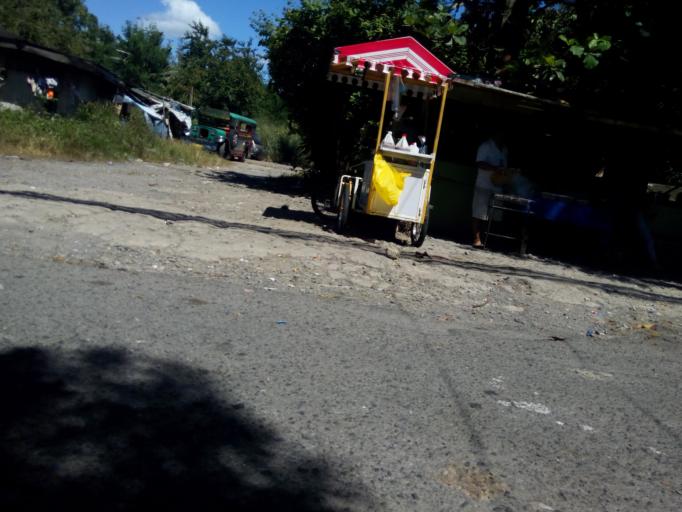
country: PH
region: Metro Manila
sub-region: Quezon City
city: Quezon City
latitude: 14.6452
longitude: 121.0692
